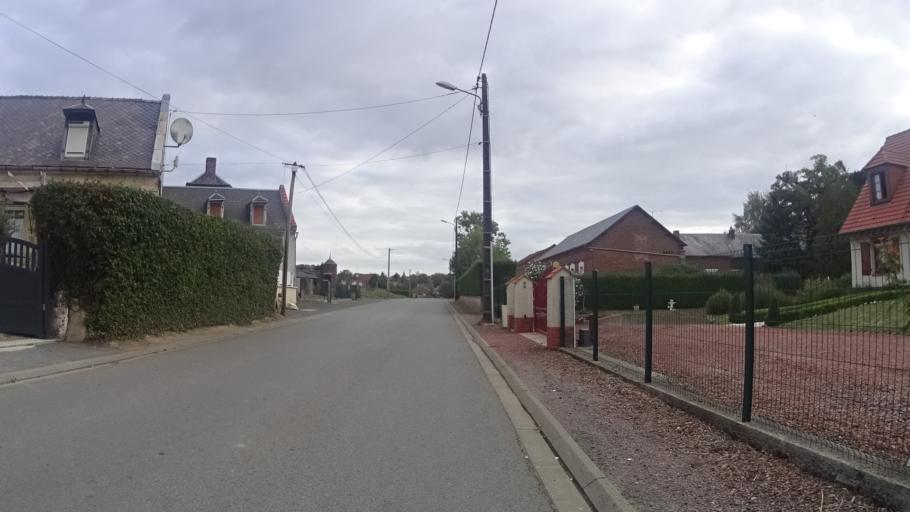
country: FR
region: Picardie
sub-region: Departement de l'Aisne
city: Guise
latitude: 49.9310
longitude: 3.5798
